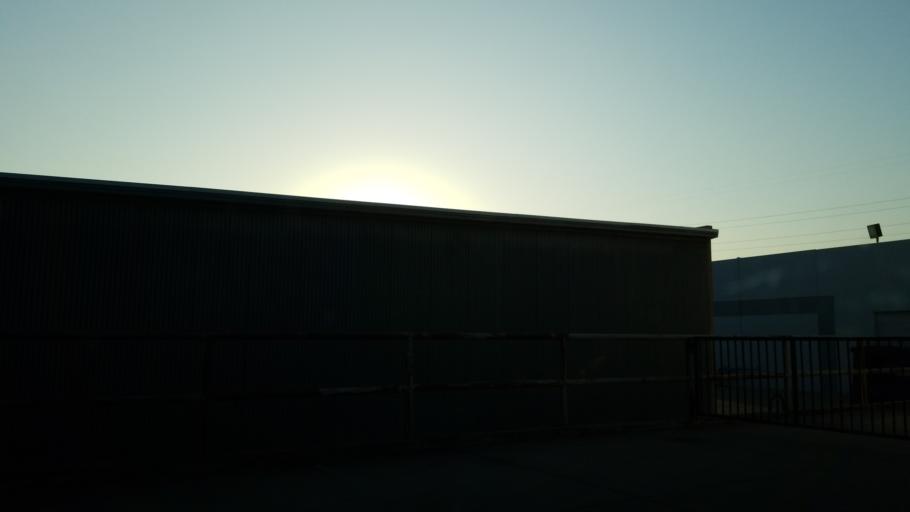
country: US
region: Texas
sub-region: Dallas County
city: Farmers Branch
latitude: 32.8829
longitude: -96.8885
